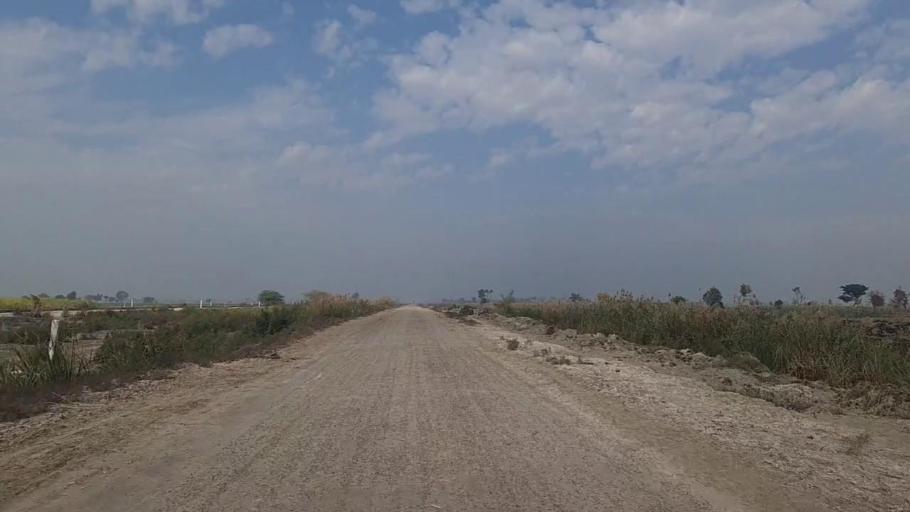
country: PK
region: Sindh
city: Daur
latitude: 26.3853
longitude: 68.3526
